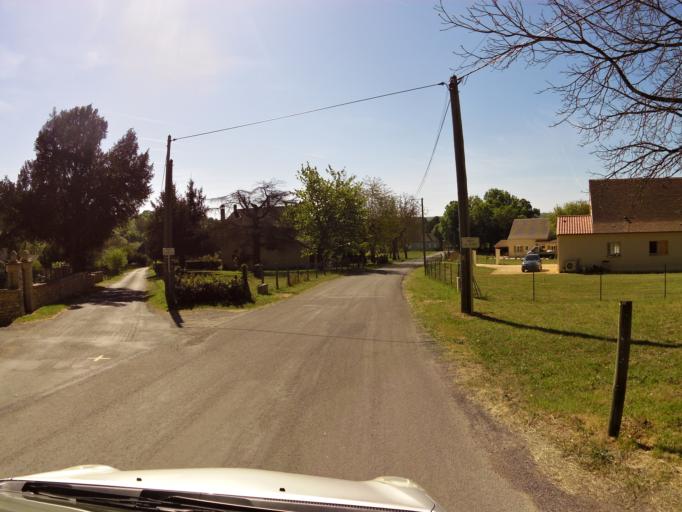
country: FR
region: Aquitaine
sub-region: Departement de la Dordogne
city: Carsac-Aillac
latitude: 44.8395
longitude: 1.2278
